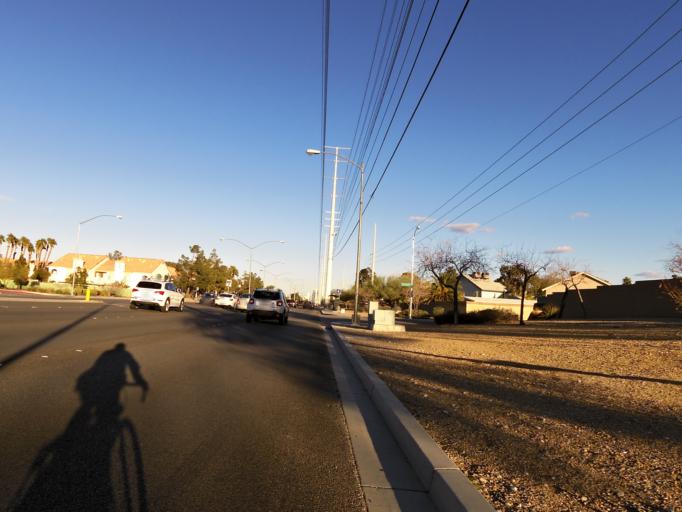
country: US
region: Nevada
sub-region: Clark County
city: Spring Valley
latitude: 36.1145
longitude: -115.2576
